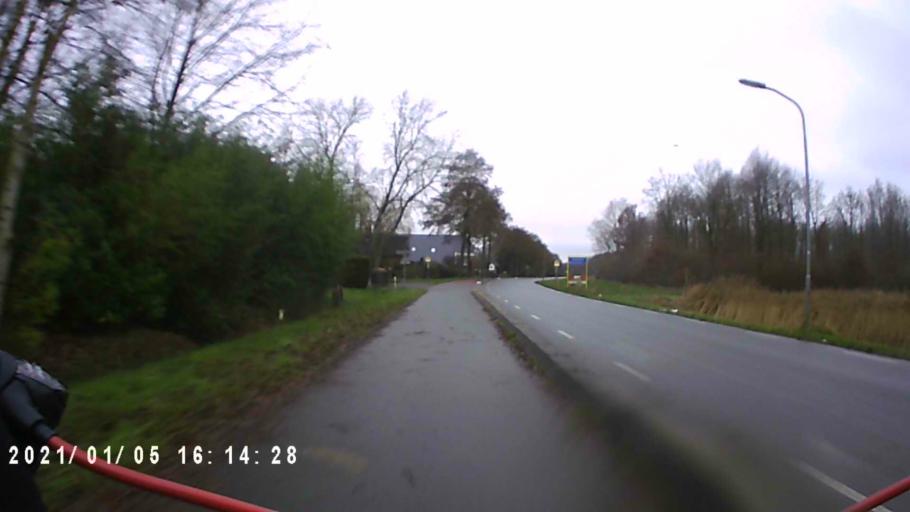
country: NL
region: Groningen
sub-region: Gemeente  Oldambt
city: Winschoten
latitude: 53.1933
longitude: 7.0644
